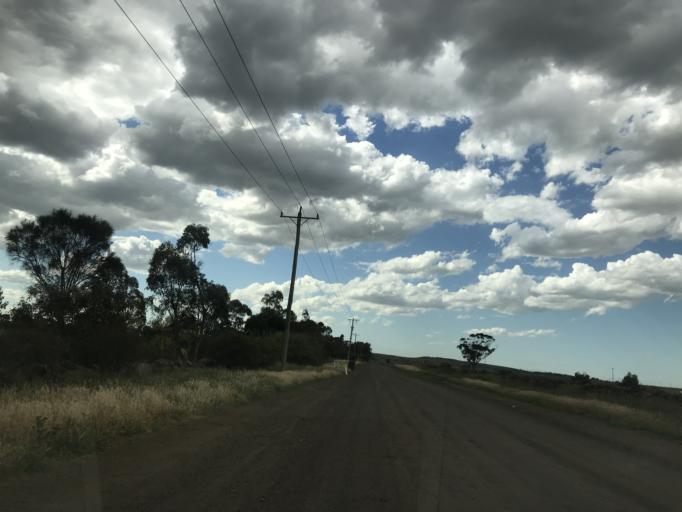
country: AU
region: Victoria
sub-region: Wyndham
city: Truganina
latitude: -37.8115
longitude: 144.7228
